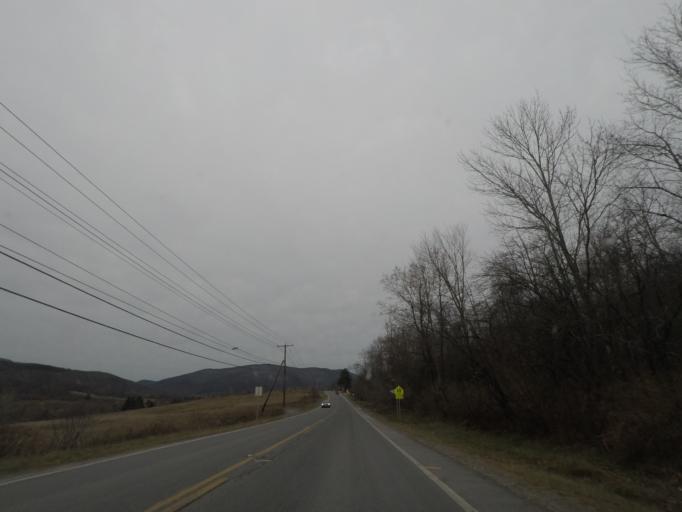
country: US
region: Massachusetts
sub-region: Berkshire County
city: Williamstown
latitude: 42.6745
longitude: -73.2359
